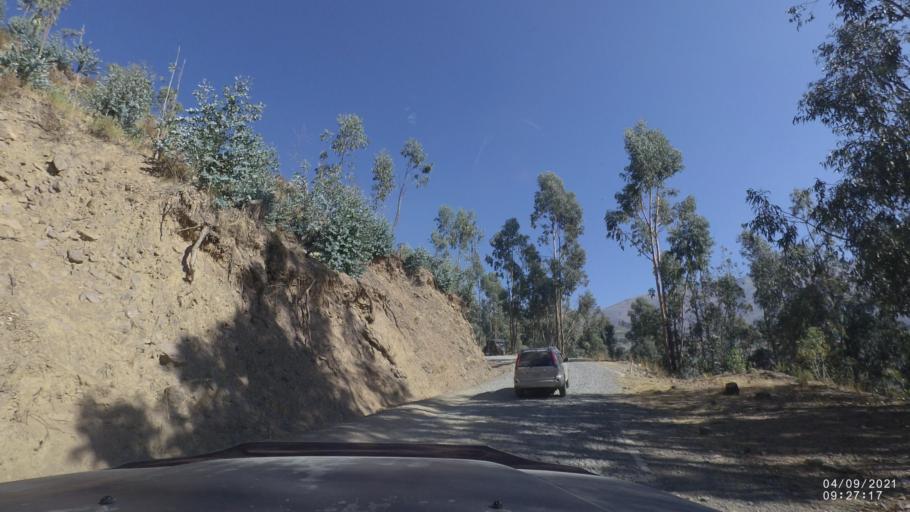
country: BO
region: Cochabamba
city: Sipe Sipe
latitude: -17.3576
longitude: -66.3721
